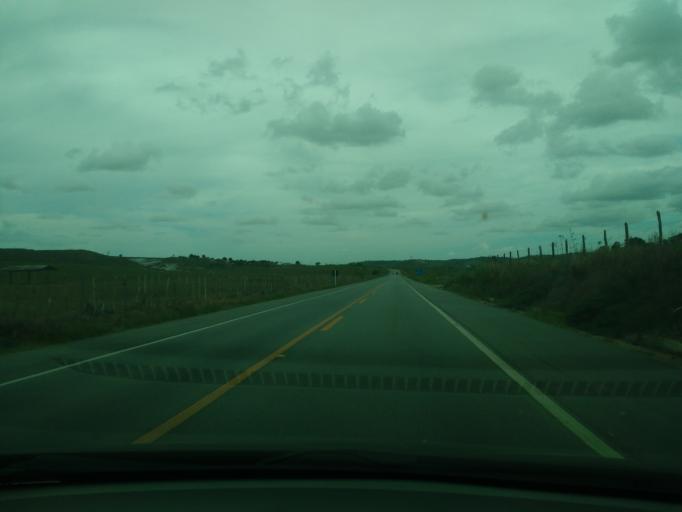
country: BR
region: Alagoas
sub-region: Murici
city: Murici
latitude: -9.2917
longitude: -35.9605
